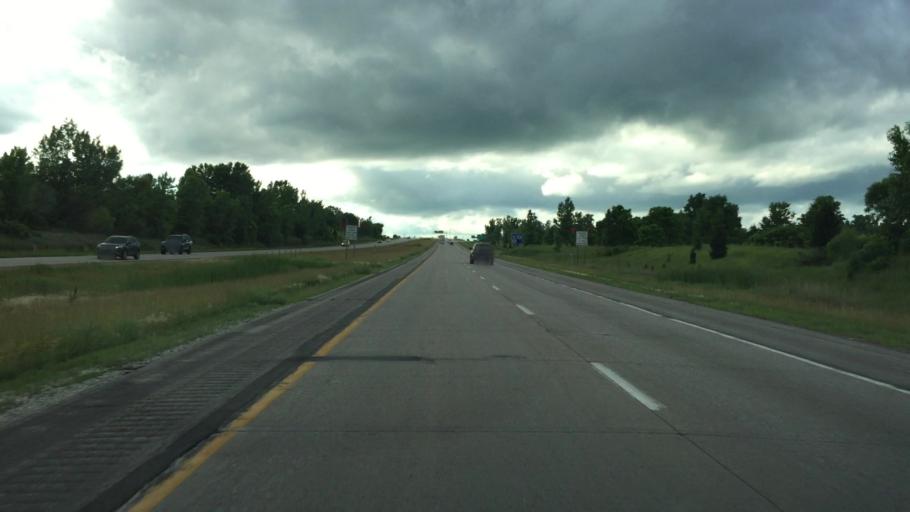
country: US
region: Iowa
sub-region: Polk County
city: Altoona
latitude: 41.6347
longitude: -93.5041
